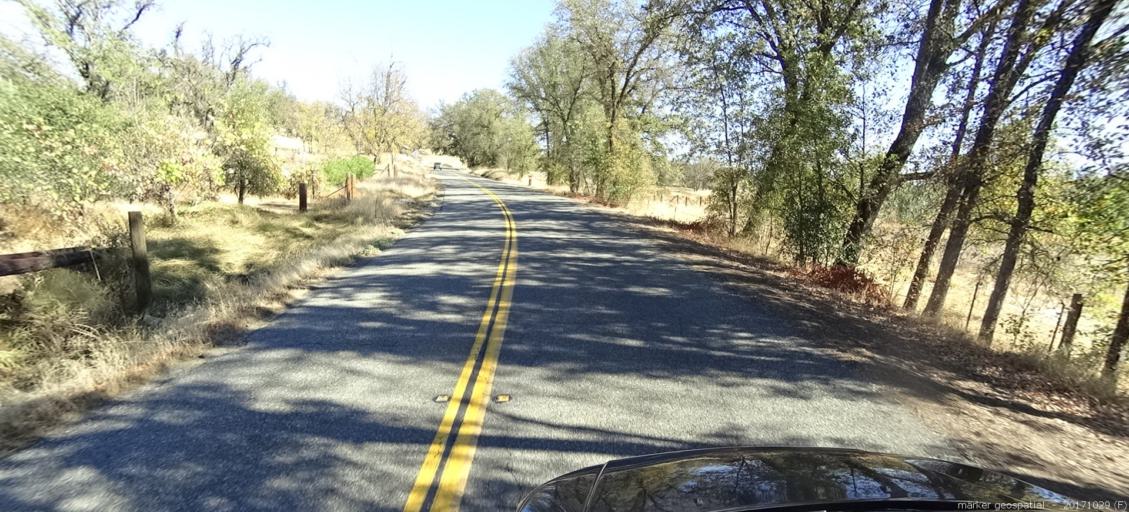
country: US
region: California
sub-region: Shasta County
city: Shasta
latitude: 40.4819
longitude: -122.5768
